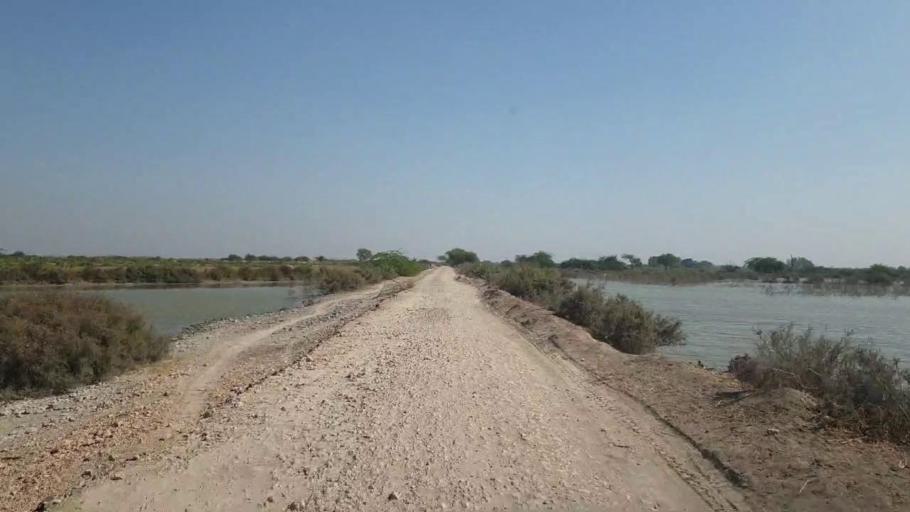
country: PK
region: Sindh
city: Talhar
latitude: 24.7759
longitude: 68.7820
